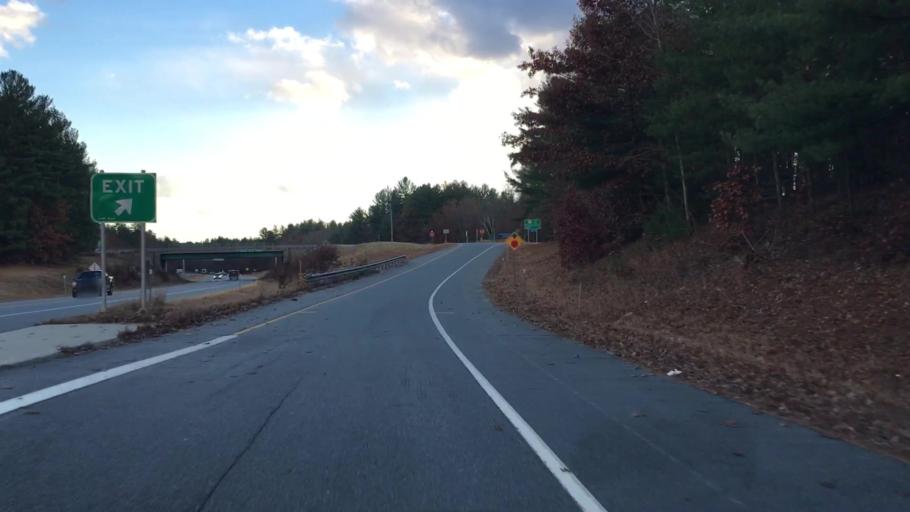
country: US
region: New Hampshire
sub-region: Hillsborough County
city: Milford
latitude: 42.8680
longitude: -71.6139
